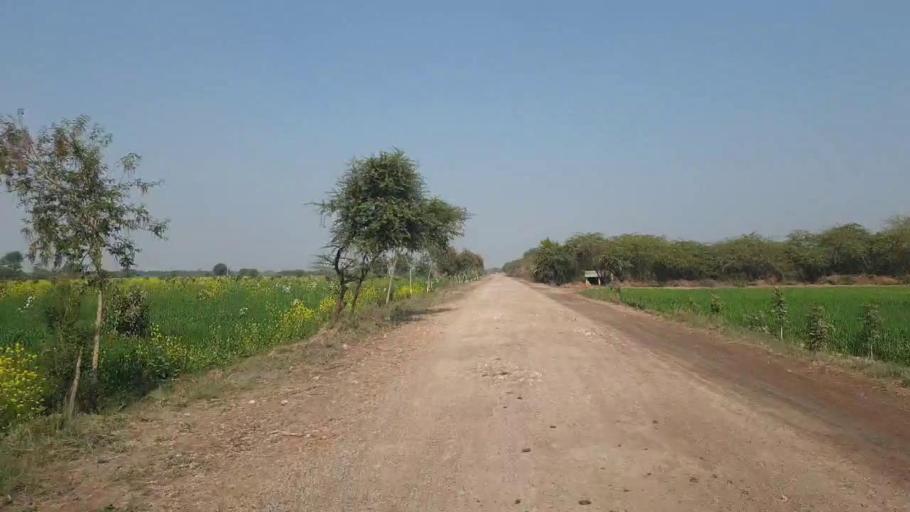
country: PK
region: Sindh
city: Mirwah Gorchani
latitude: 25.3728
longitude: 68.9317
